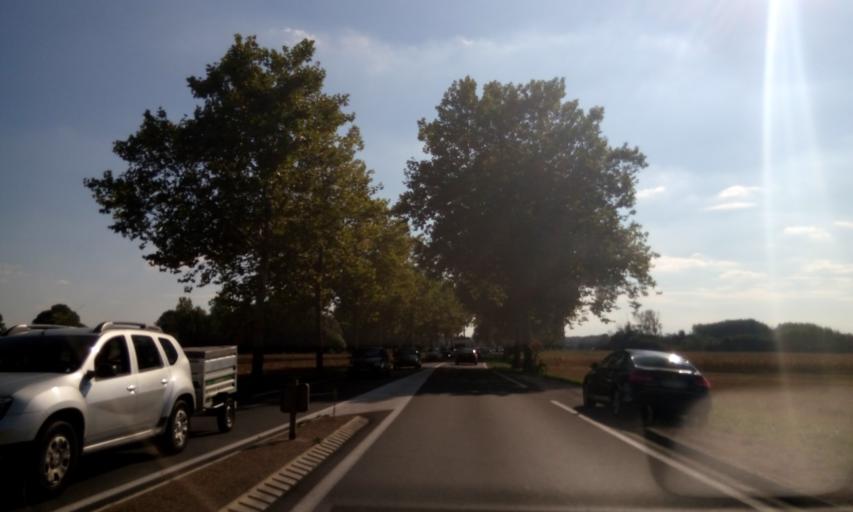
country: FR
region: Centre
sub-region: Departement d'Indre-et-Loire
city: Poce-sur-Cisse
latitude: 47.4448
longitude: 1.0080
